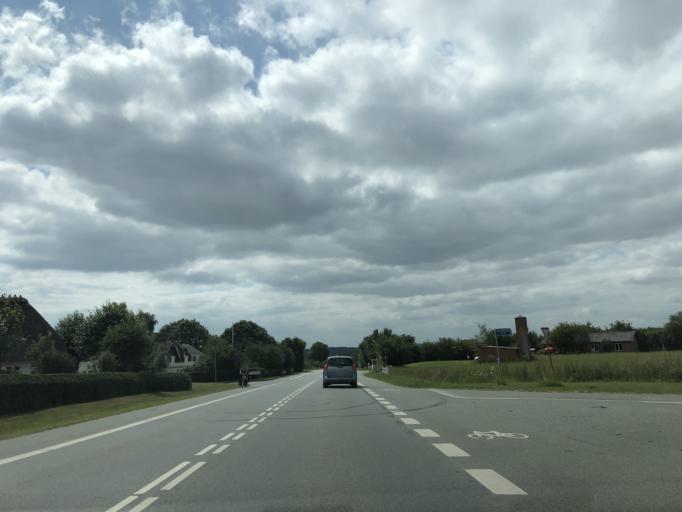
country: DK
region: South Denmark
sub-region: Sonderborg Kommune
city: Augustenborg
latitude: 54.9603
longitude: 9.9177
